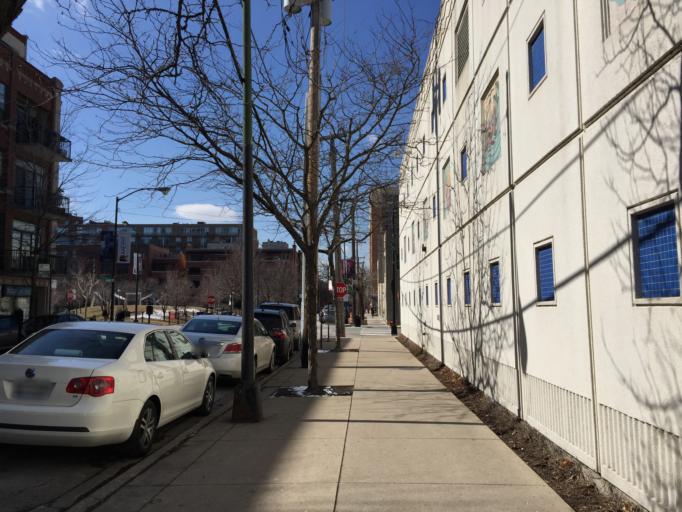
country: US
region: Illinois
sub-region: Cook County
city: Chicago
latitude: 41.8805
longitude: -87.6491
